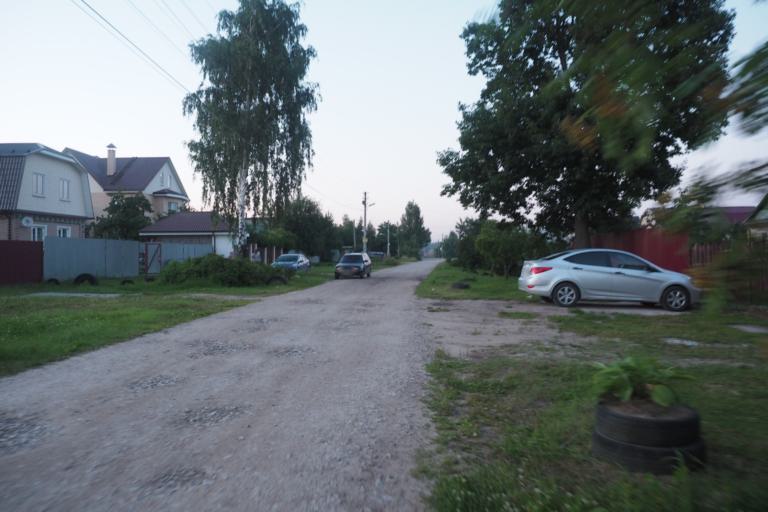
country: RU
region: Moskovskaya
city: Ramenskoye
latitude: 55.5563
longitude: 38.3066
